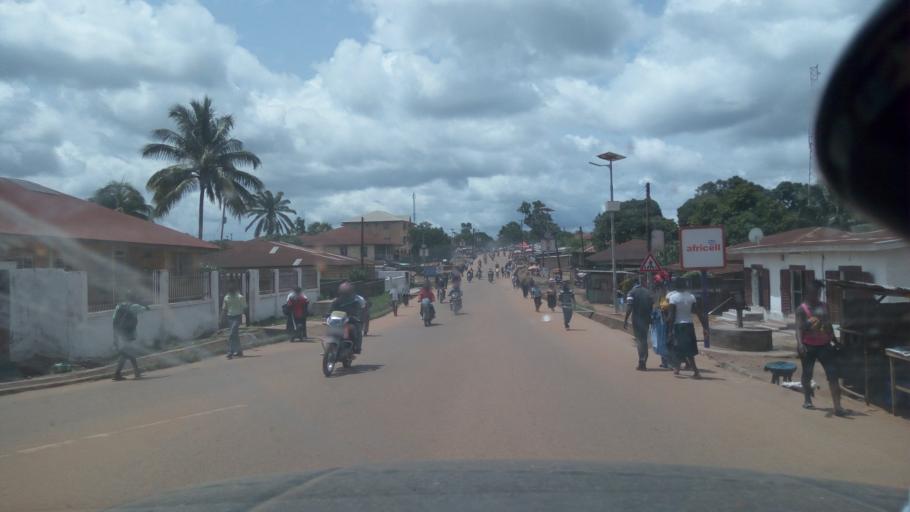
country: SL
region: Eastern Province
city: Kenema
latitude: 7.8766
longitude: -11.1870
